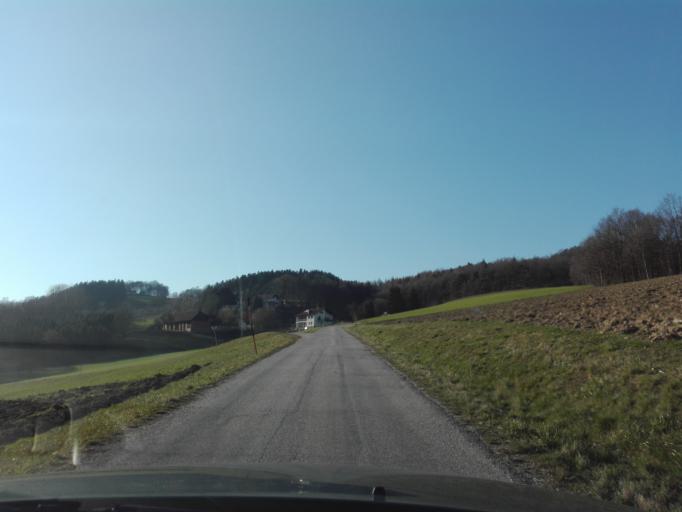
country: AT
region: Upper Austria
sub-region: Politischer Bezirk Rohrbach
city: Kleinzell im Muehlkreis
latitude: 48.3795
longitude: 13.9640
